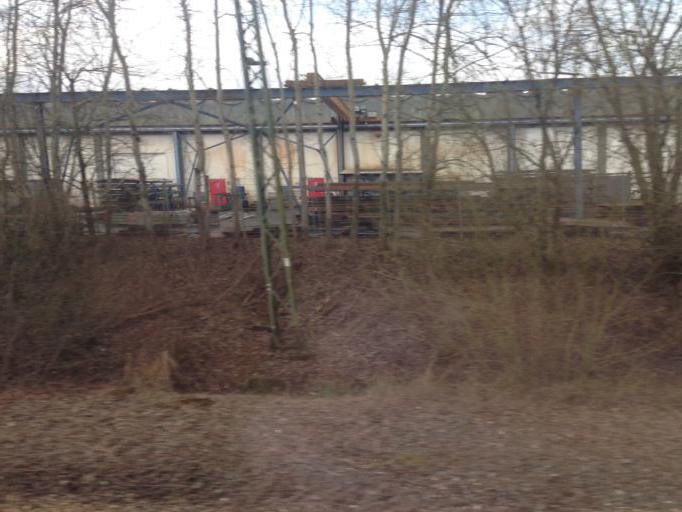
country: DE
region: North Rhine-Westphalia
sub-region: Regierungsbezirk Munster
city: Nottuln
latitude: 51.8664
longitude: 7.3825
